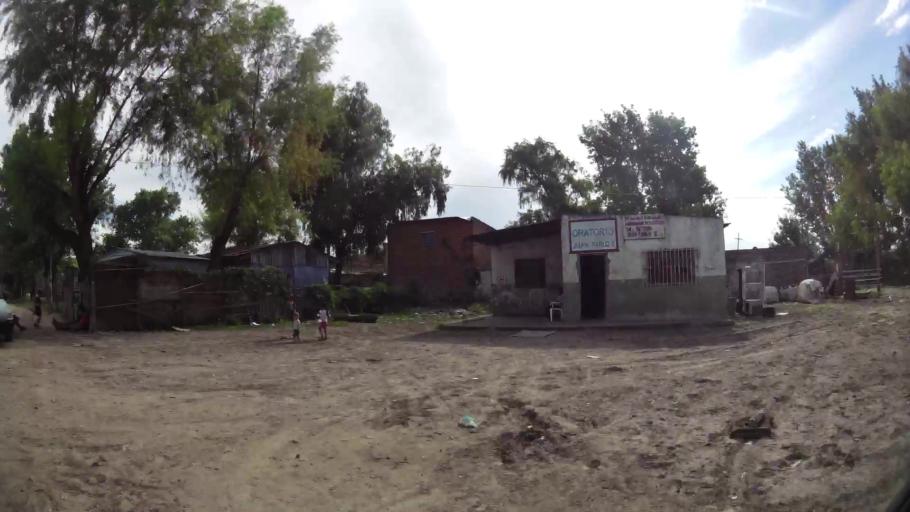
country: AR
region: Santa Fe
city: Granadero Baigorria
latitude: -32.9093
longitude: -60.7058
